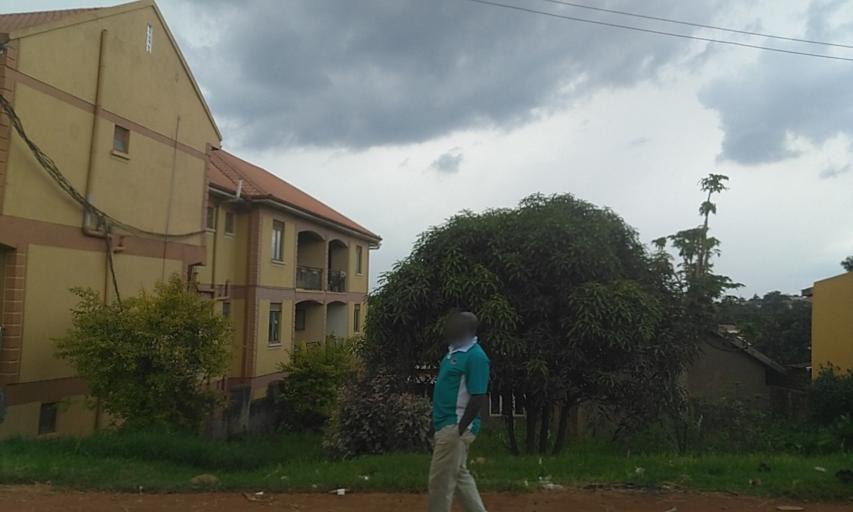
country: UG
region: Central Region
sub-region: Wakiso District
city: Wakiso
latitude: 0.3324
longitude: 32.4936
